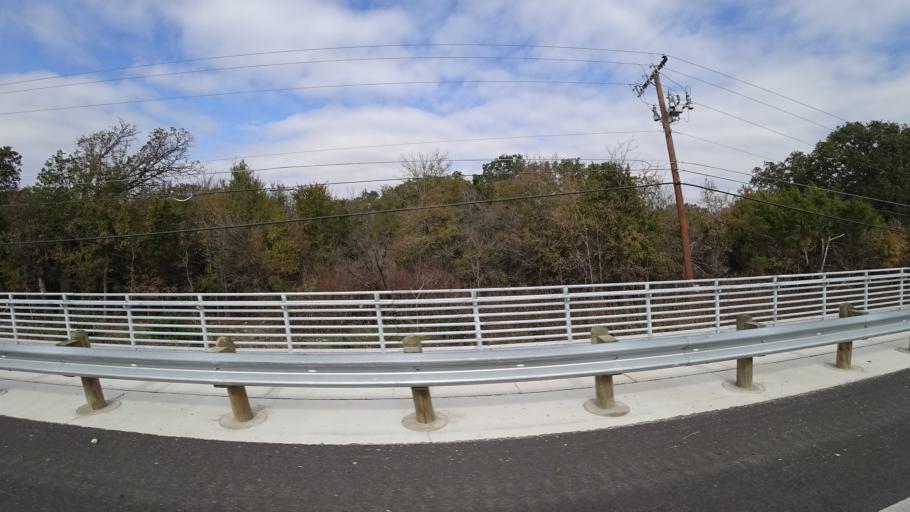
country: US
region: Texas
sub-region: Williamson County
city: Round Rock
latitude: 30.5339
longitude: -97.7026
